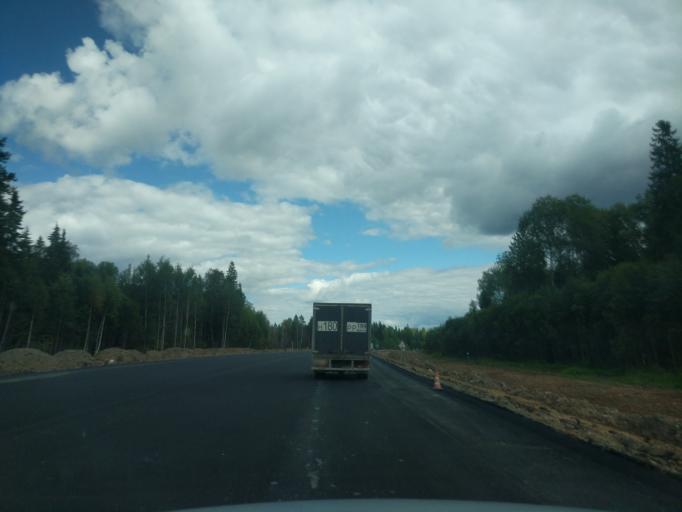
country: RU
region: Kostroma
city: Sudislavl'
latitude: 57.8257
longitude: 41.5015
